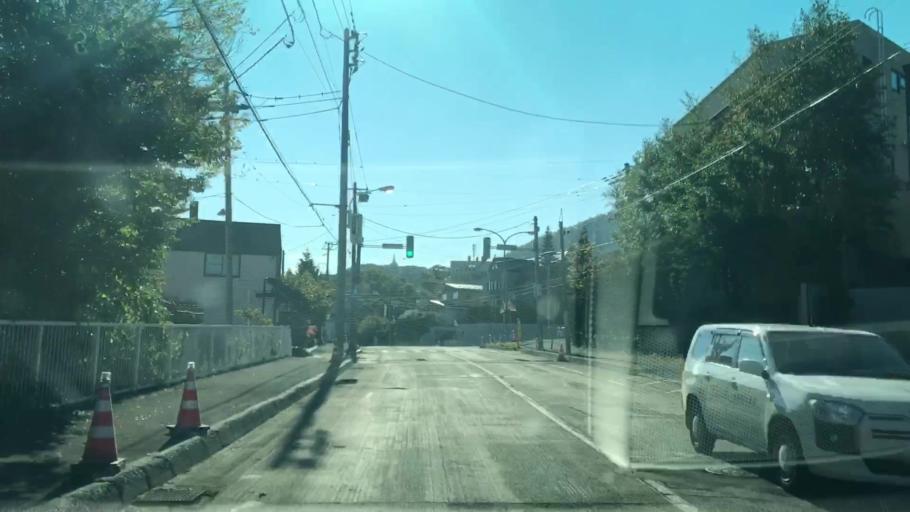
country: JP
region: Hokkaido
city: Sapporo
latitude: 43.0391
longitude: 141.3216
